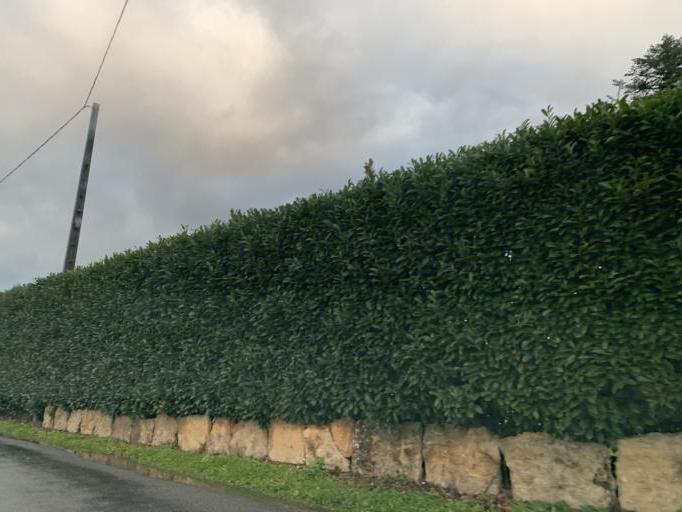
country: FR
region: Rhone-Alpes
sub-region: Departement de l'Ain
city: Belley
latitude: 45.8018
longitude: 5.6927
